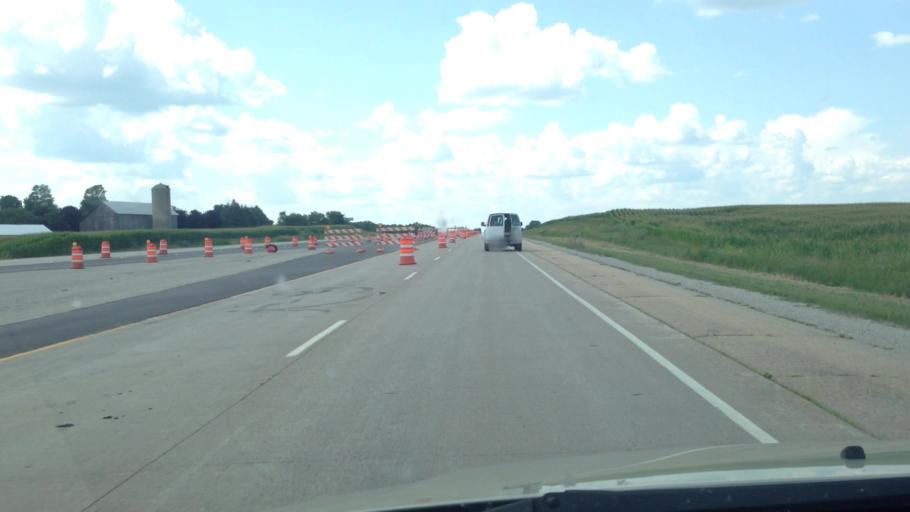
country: US
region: Wisconsin
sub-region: Brown County
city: Pulaski
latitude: 44.6906
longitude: -88.3287
